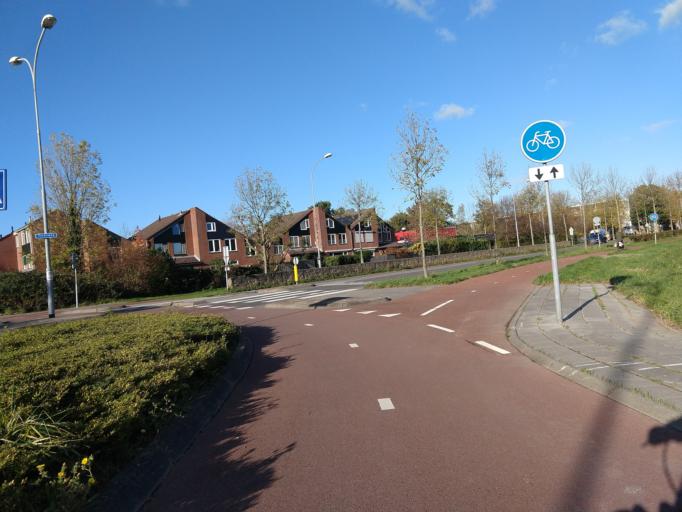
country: NL
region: Zeeland
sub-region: Gemeente Middelburg
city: Middelburg
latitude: 51.4863
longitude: 3.6293
